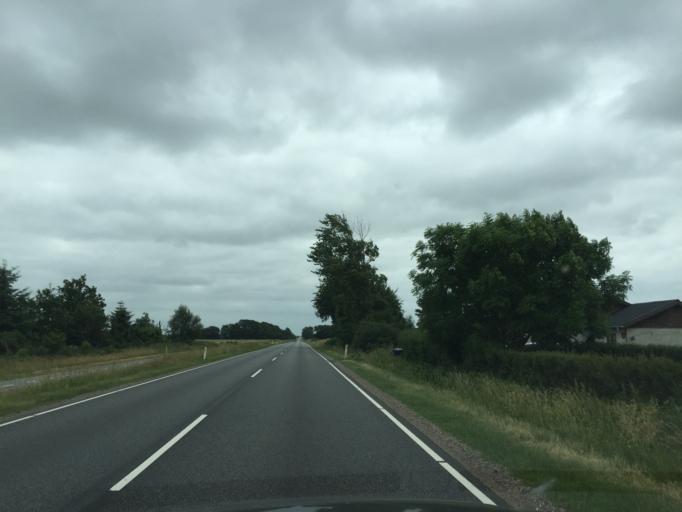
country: DK
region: South Denmark
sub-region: Esbjerg Kommune
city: Ribe
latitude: 55.2608
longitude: 8.7222
